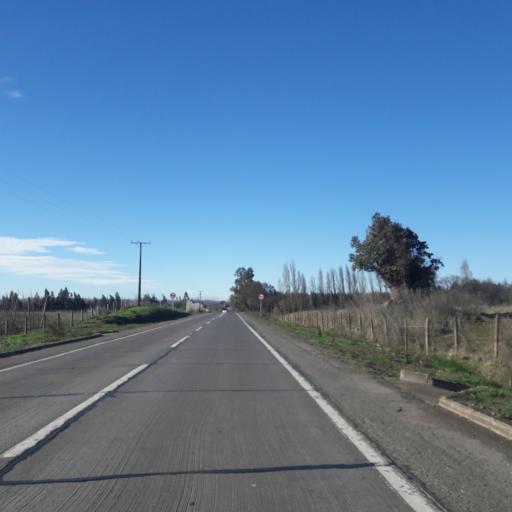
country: CL
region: Araucania
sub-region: Provincia de Malleco
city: Angol
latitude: -37.7478
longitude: -72.5929
